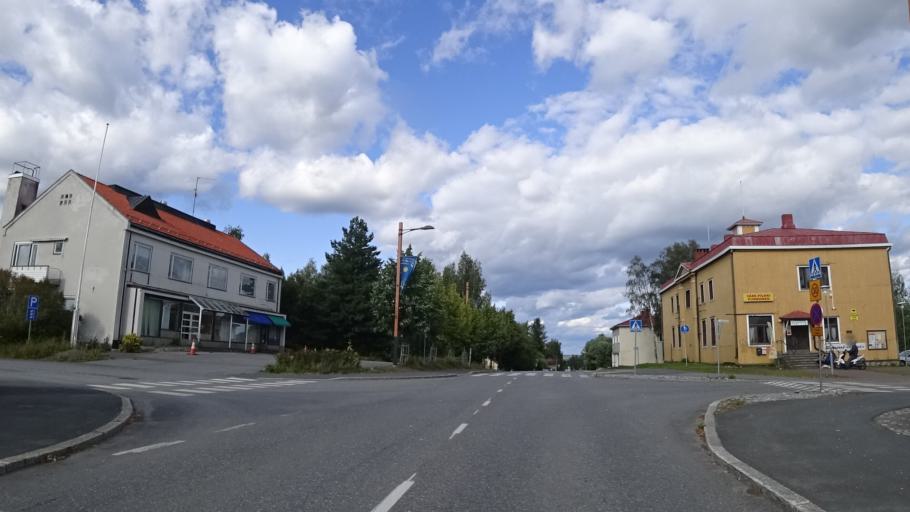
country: FI
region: North Karelia
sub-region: Keski-Karjala
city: Tohmajaervi
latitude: 62.2249
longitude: 30.3305
